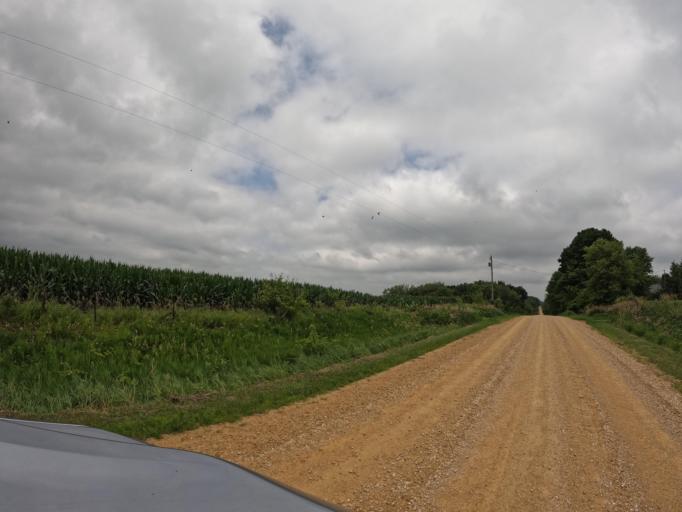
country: US
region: Illinois
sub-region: Carroll County
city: Savanna
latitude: 42.0119
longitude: -90.1697
